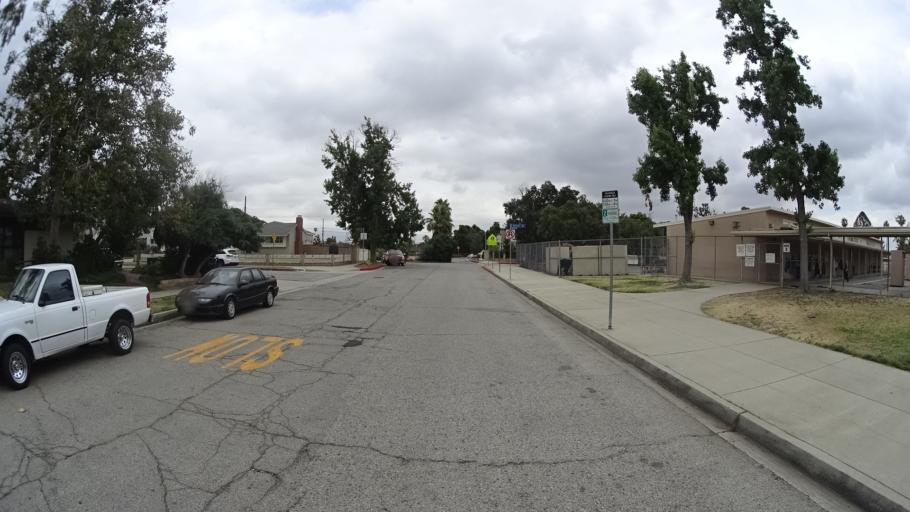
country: US
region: California
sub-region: Los Angeles County
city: San Fernando
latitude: 34.2626
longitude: -118.4572
